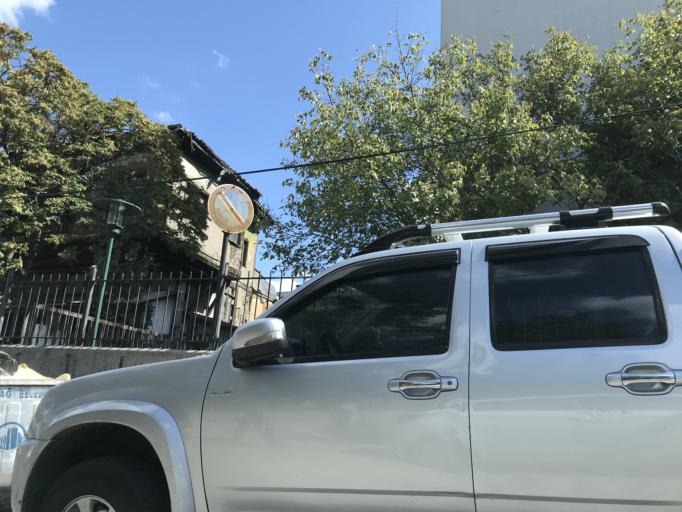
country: TR
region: Ankara
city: Ankara
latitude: 39.9343
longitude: 32.8580
